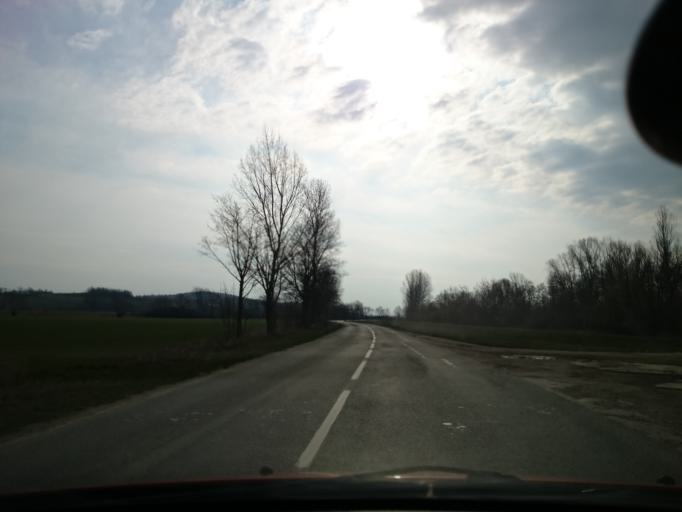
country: PL
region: Lower Silesian Voivodeship
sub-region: Powiat zabkowicki
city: Kamieniec Zabkowicki
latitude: 50.5119
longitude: 16.9265
